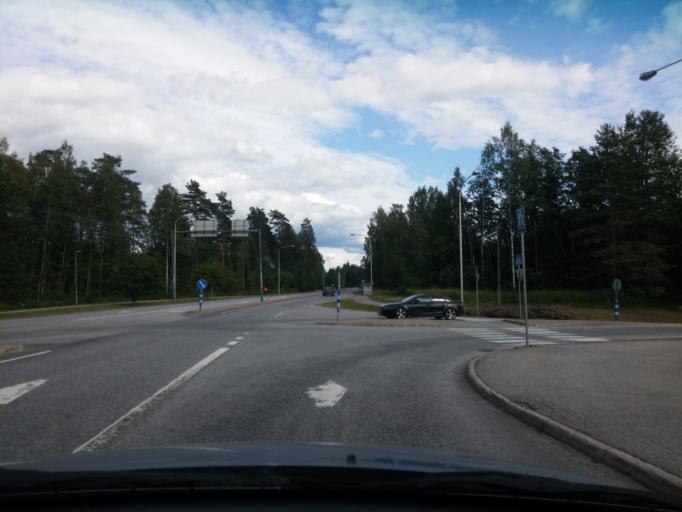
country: FI
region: Central Finland
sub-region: Keuruu
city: Keuruu
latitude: 62.2544
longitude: 24.7204
